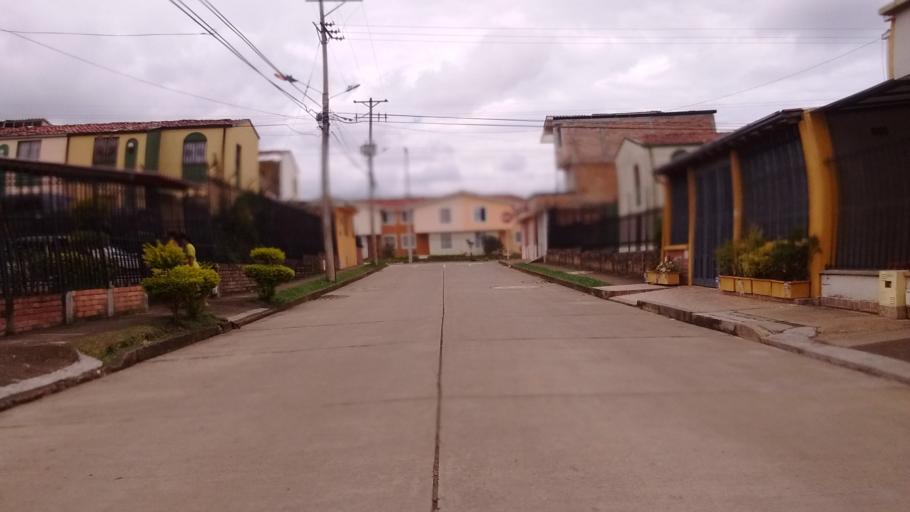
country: CO
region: Cauca
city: Popayan
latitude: 2.4800
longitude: -76.5800
